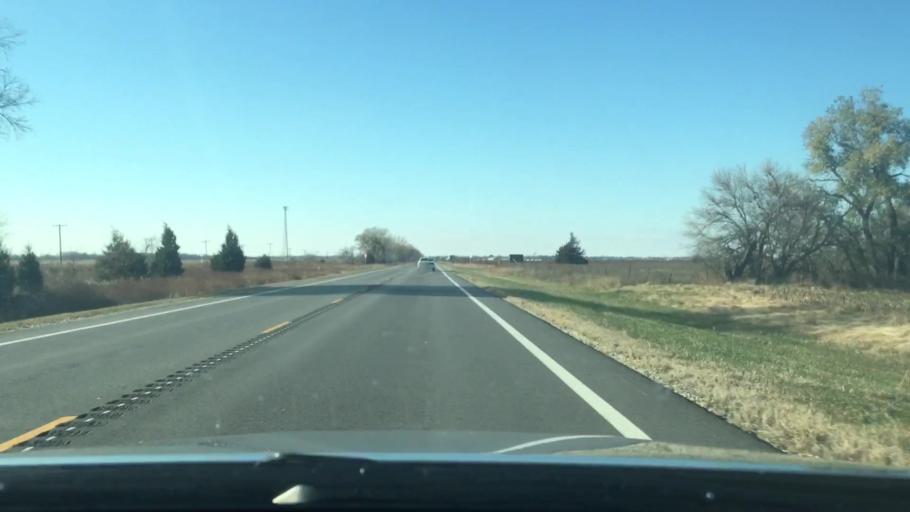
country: US
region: Kansas
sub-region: Reno County
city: Nickerson
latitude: 38.1234
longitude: -98.0486
